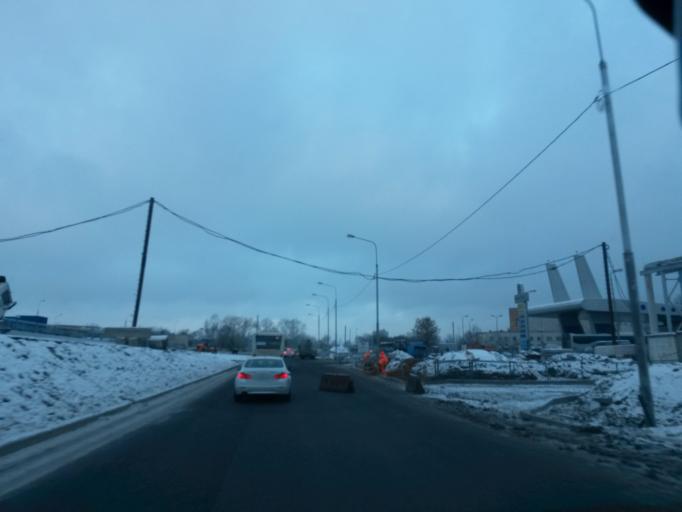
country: RU
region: Moscow
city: Mikhalkovo
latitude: 55.6773
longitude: 37.4366
